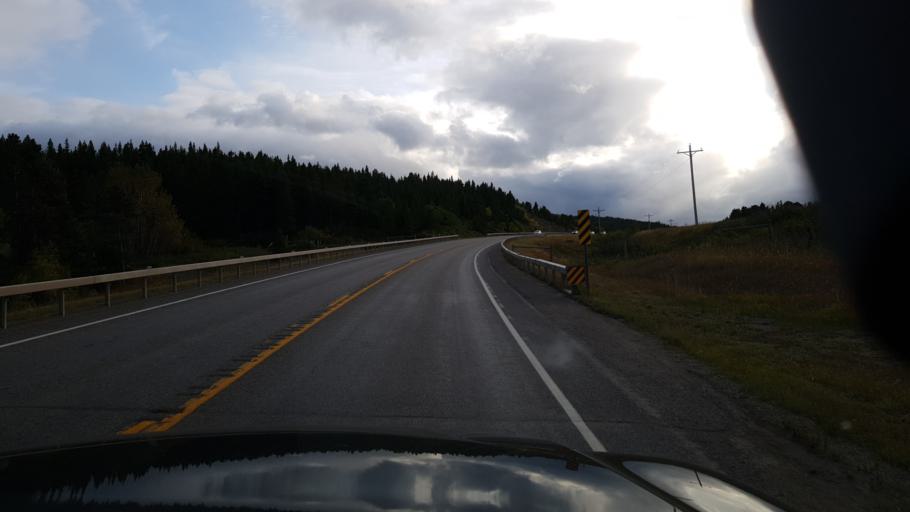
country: US
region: Montana
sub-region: Glacier County
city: South Browning
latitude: 48.3918
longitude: -113.2579
